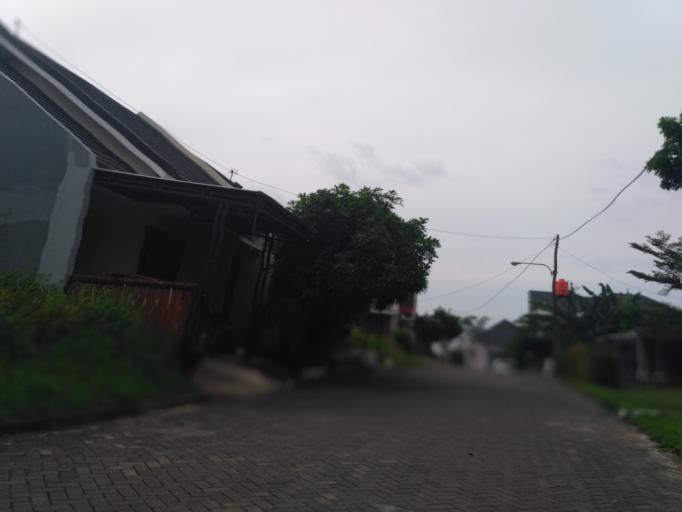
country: ID
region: Central Java
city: Ungaran
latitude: -7.0780
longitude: 110.4236
